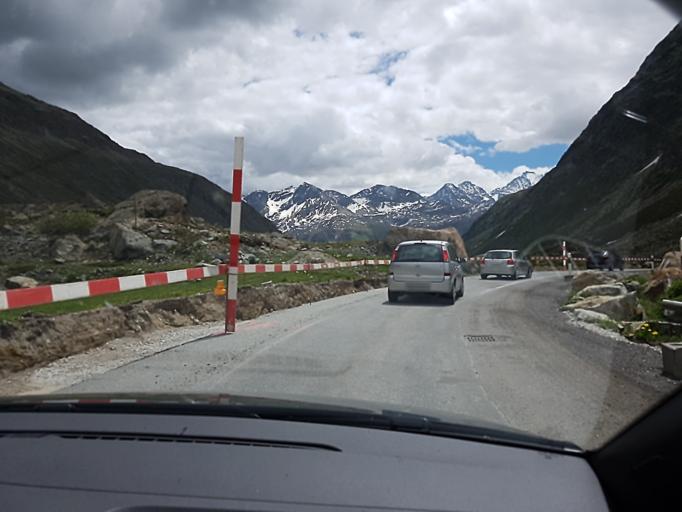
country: CH
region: Grisons
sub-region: Maloja District
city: Silvaplana
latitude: 46.4725
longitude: 9.7495
